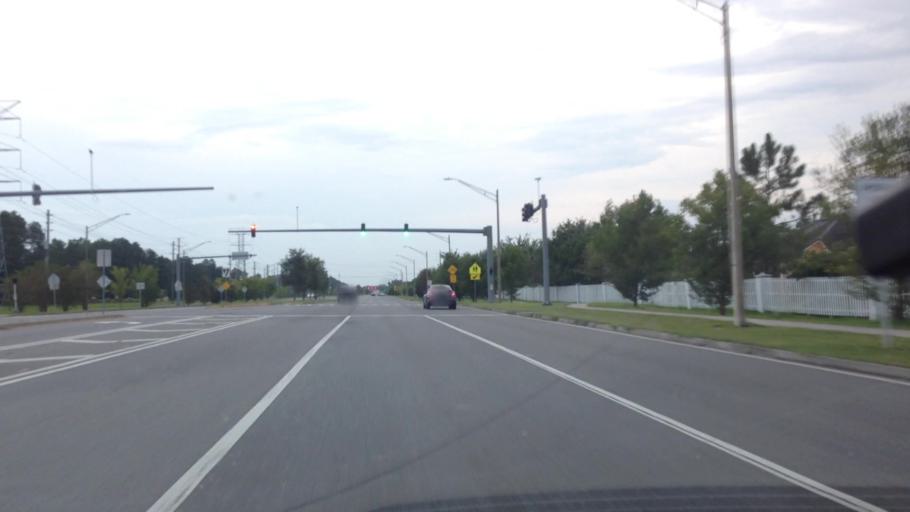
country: US
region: Florida
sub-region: Duval County
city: Neptune Beach
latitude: 30.3049
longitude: -81.4892
